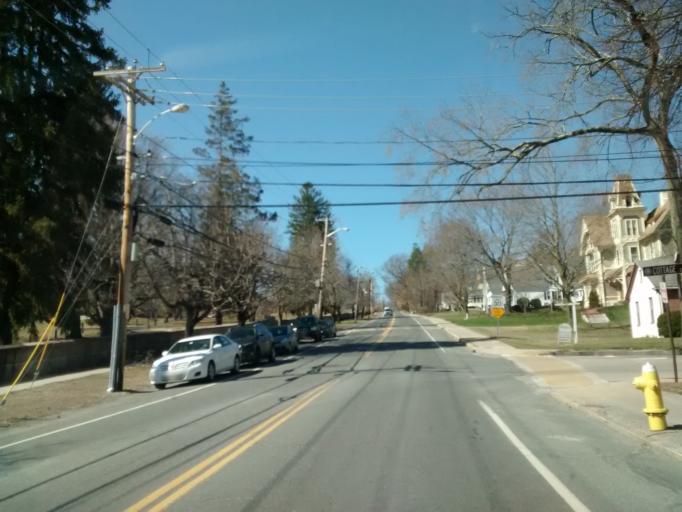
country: US
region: Massachusetts
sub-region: Worcester County
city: Whitinsville
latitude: 42.1111
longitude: -71.6654
